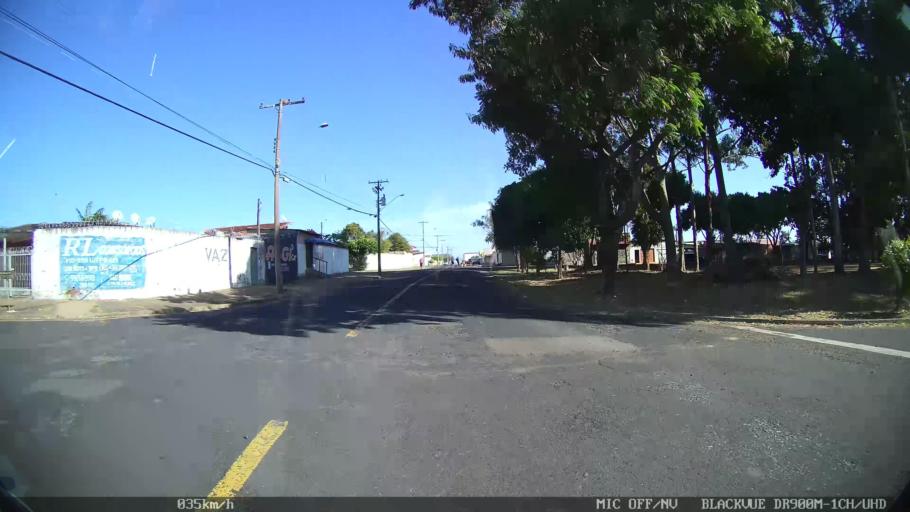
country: BR
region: Sao Paulo
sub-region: Franca
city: Franca
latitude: -20.4955
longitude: -47.4178
